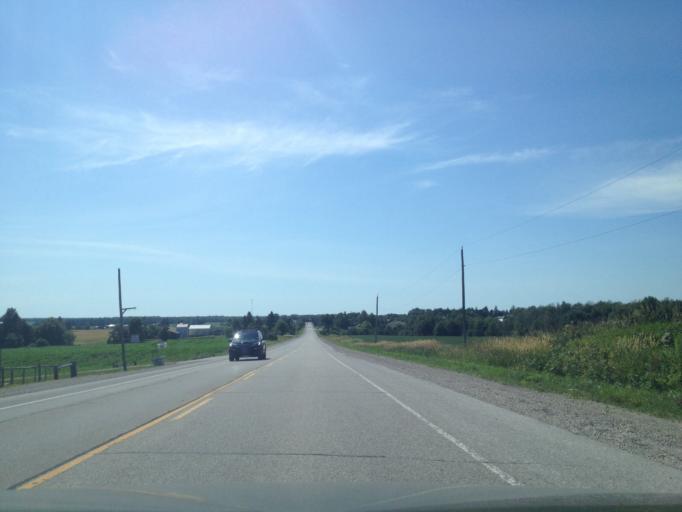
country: CA
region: Ontario
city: Waterloo
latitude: 43.5262
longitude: -80.7279
